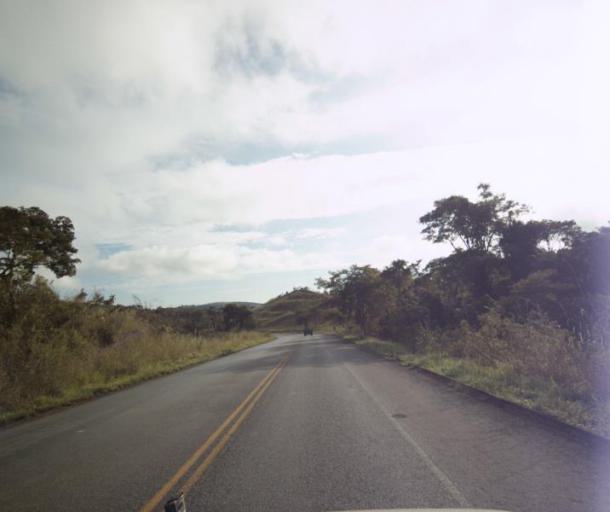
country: BR
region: Goias
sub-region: Pirenopolis
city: Pirenopolis
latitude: -15.7187
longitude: -48.6965
